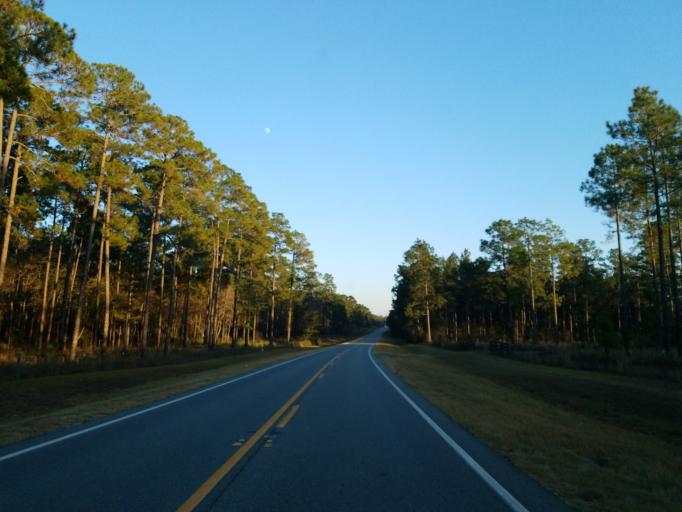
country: US
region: Georgia
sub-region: Wilcox County
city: Rochelle
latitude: 31.8221
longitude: -83.5443
